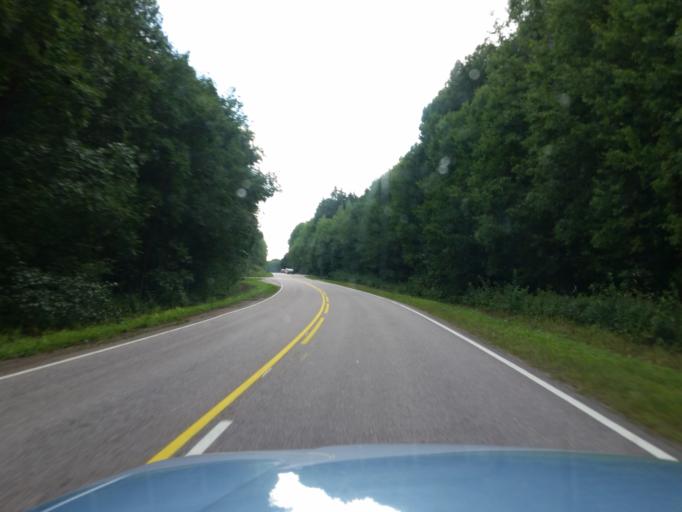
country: FI
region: Varsinais-Suomi
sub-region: Aboland-Turunmaa
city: Nagu
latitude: 60.2187
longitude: 22.0903
